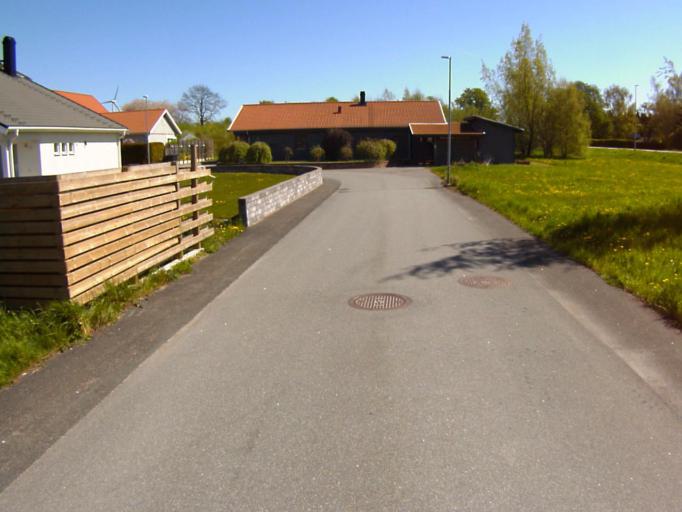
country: SE
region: Skane
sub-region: Kristianstads Kommun
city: Kristianstad
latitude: 56.0485
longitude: 14.2164
